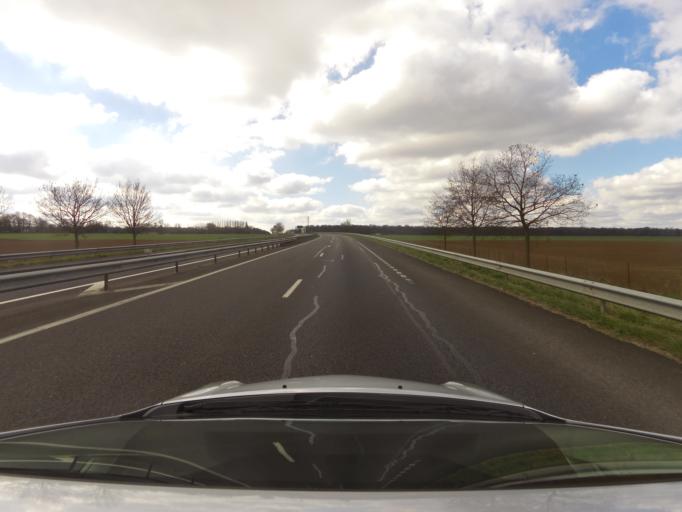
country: FR
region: Picardie
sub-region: Departement de la Somme
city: Bouttencourt
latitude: 49.9539
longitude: 1.6490
